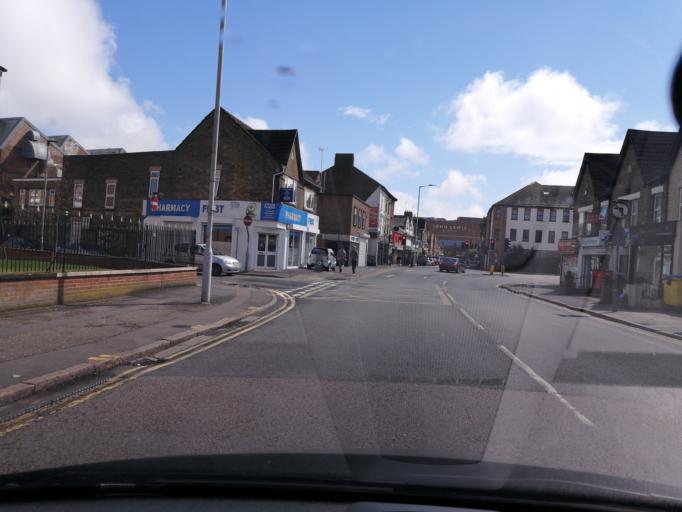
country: GB
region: England
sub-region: Peterborough
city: Peterborough
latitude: 52.5773
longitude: -0.2437
